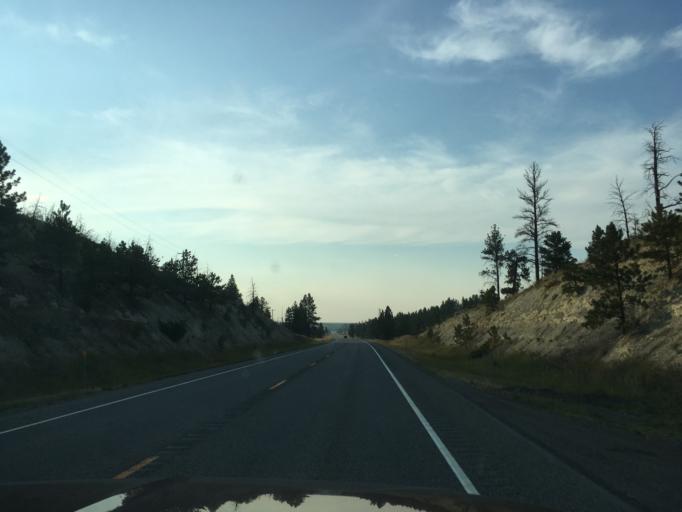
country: US
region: Montana
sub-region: Musselshell County
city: Roundup
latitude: 46.2773
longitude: -108.4746
